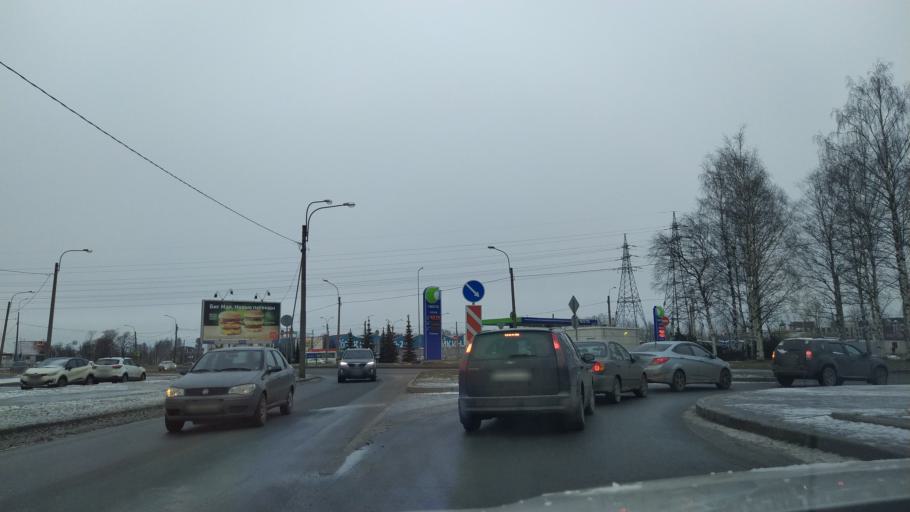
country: RU
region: St.-Petersburg
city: Grazhdanka
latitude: 60.0142
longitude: 30.4319
